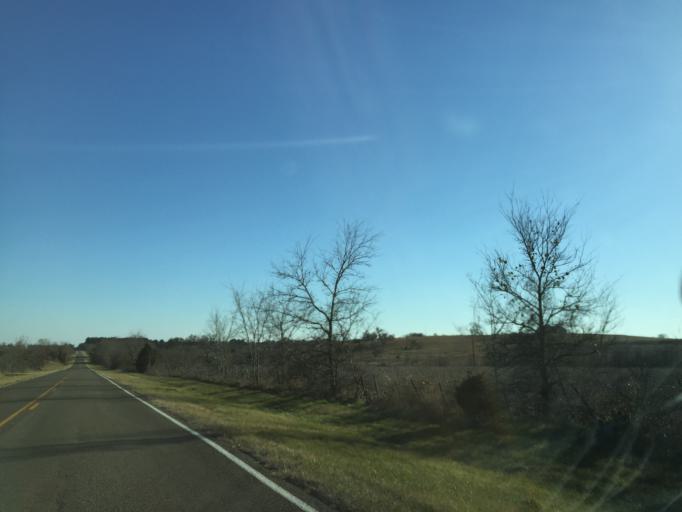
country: US
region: Texas
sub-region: Bastrop County
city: Elgin
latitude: 30.4115
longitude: -97.2541
